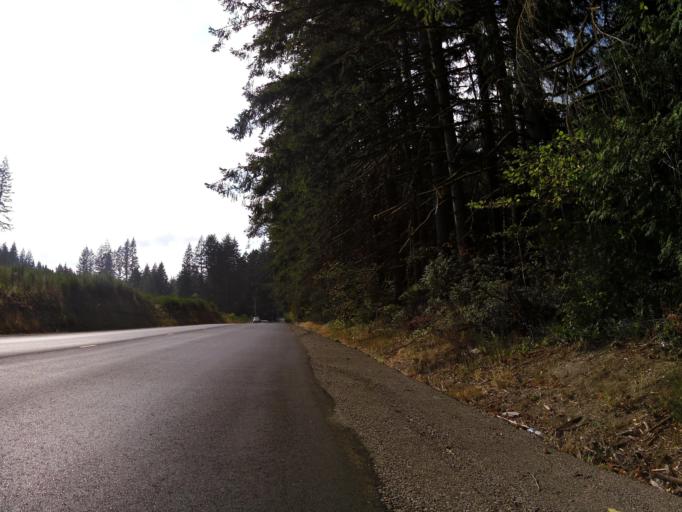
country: US
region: Washington
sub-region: Kitsap County
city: Erlands Point-Kitsap Lake
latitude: 47.5252
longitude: -122.7649
